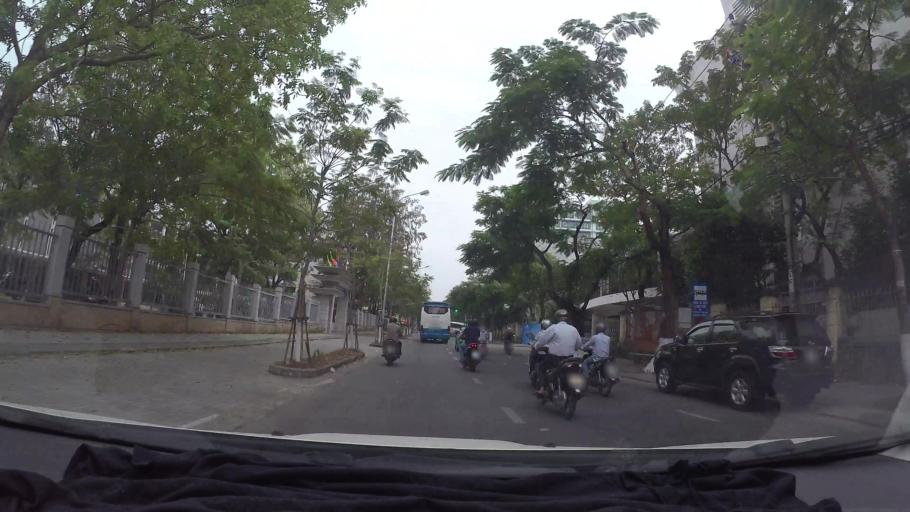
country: VN
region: Da Nang
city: Da Nang
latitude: 16.0724
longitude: 108.2202
